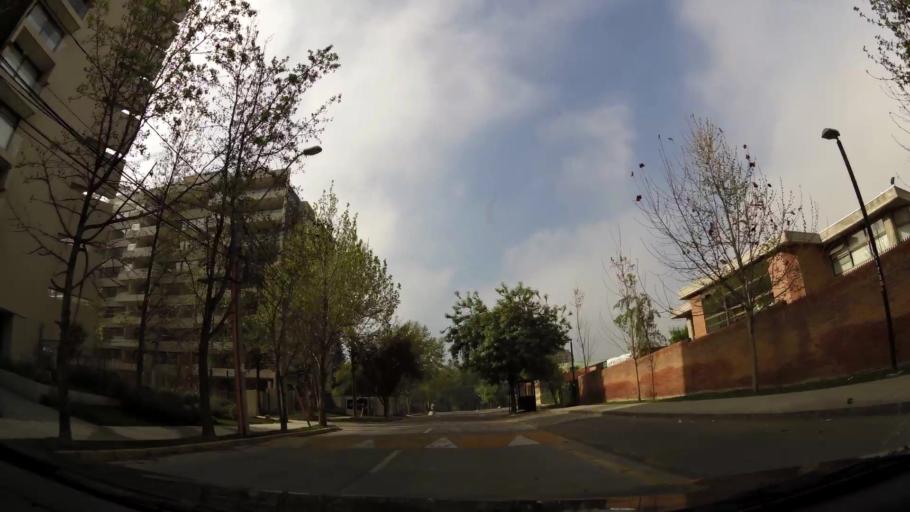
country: CL
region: Santiago Metropolitan
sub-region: Provincia de Santiago
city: Villa Presidente Frei, Nunoa, Santiago, Chile
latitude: -33.3752
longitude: -70.5265
